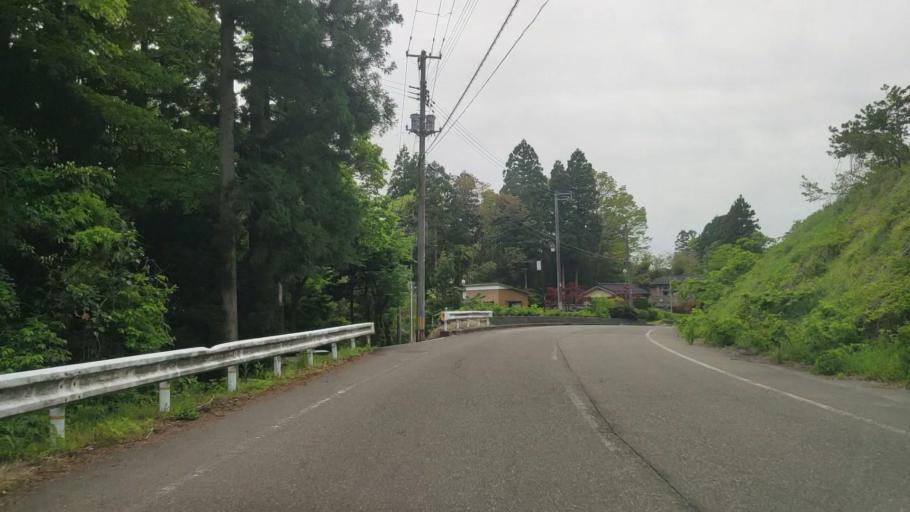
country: JP
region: Niigata
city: Kamo
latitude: 37.7143
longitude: 139.0820
